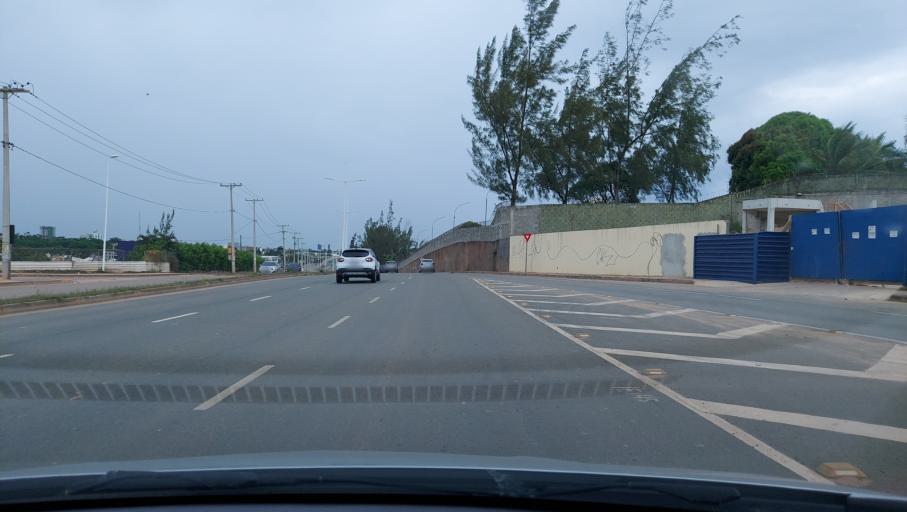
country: BR
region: Bahia
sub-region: Lauro De Freitas
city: Lauro de Freitas
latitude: -12.9405
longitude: -38.3865
